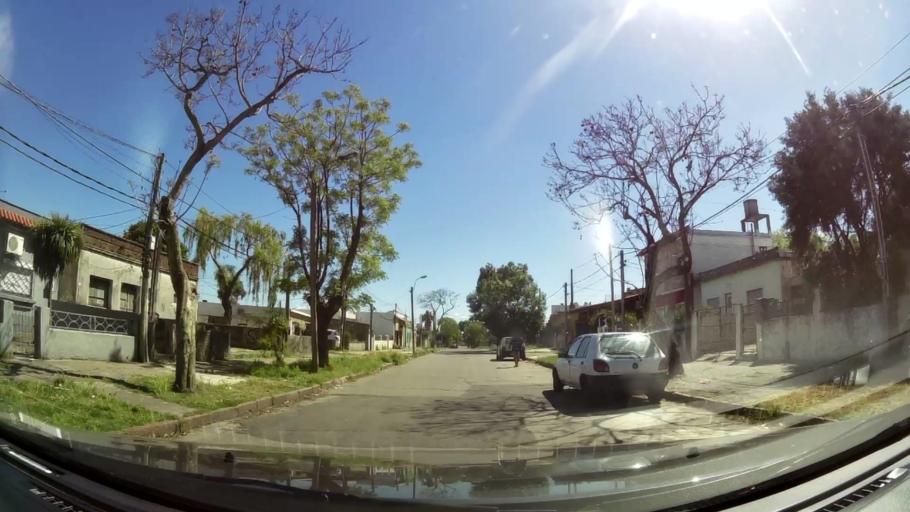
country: UY
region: Montevideo
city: Montevideo
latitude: -34.8645
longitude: -56.1265
